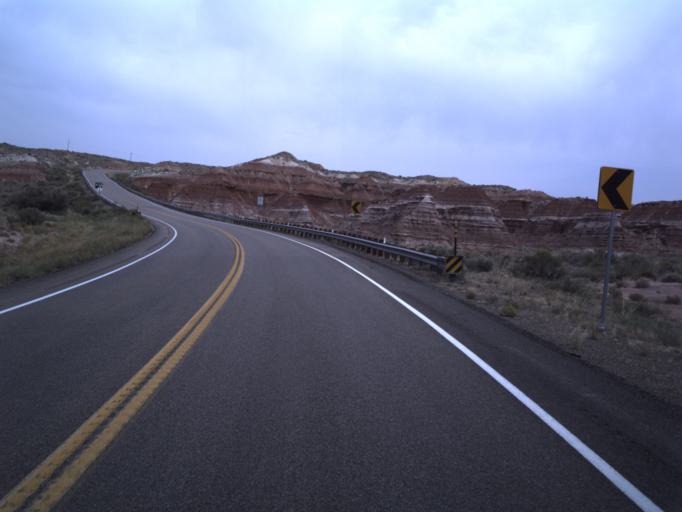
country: US
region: Arizona
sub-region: Coconino County
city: Page
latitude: 37.0998
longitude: -111.8667
